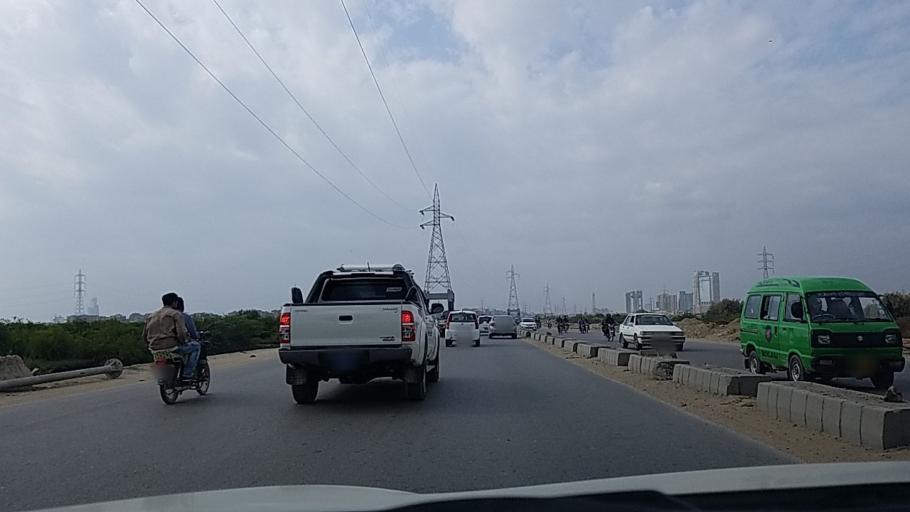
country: PK
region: Sindh
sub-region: Karachi District
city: Karachi
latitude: 24.8225
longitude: 67.0958
